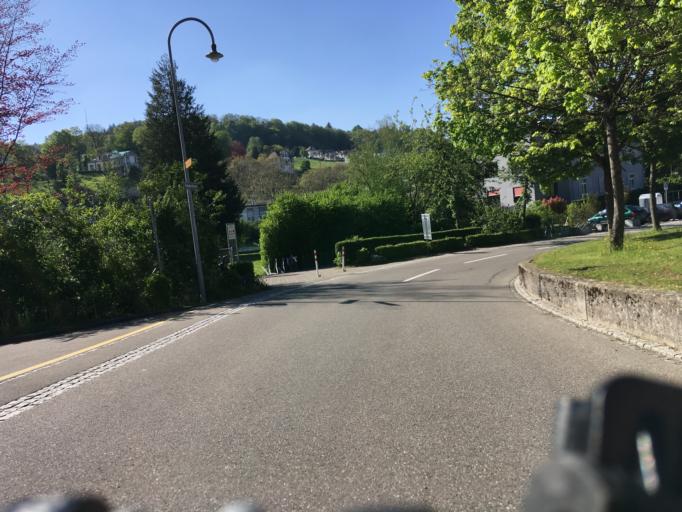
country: CH
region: Zurich
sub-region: Bezirk Andelfingen
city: Flurlingen
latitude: 47.6894
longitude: 8.6256
